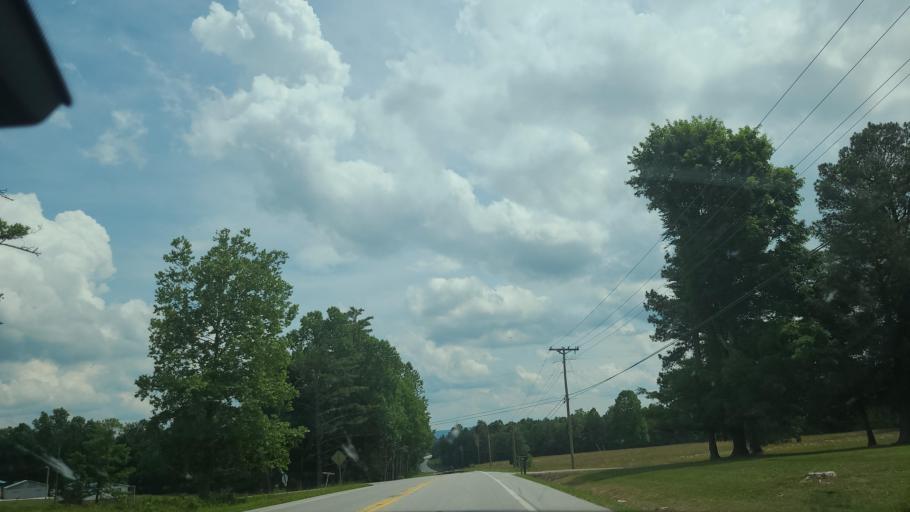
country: US
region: Tennessee
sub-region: Cumberland County
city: Lake Tansi
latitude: 35.8295
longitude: -85.0192
